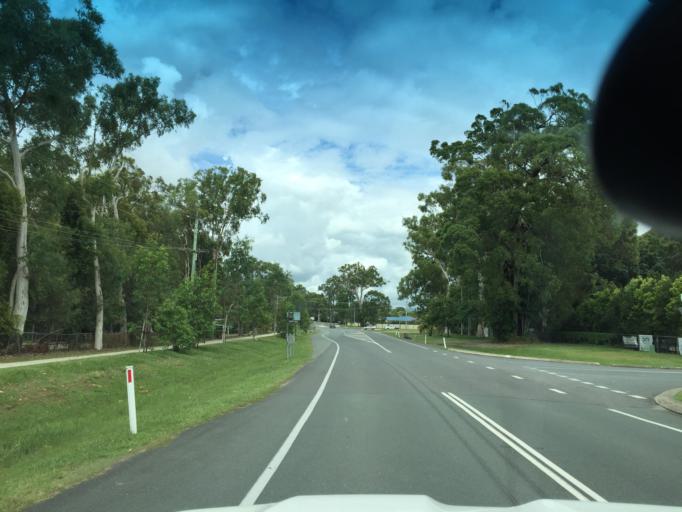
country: AU
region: Queensland
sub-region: Moreton Bay
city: Burpengary
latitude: -27.1278
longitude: 152.9891
